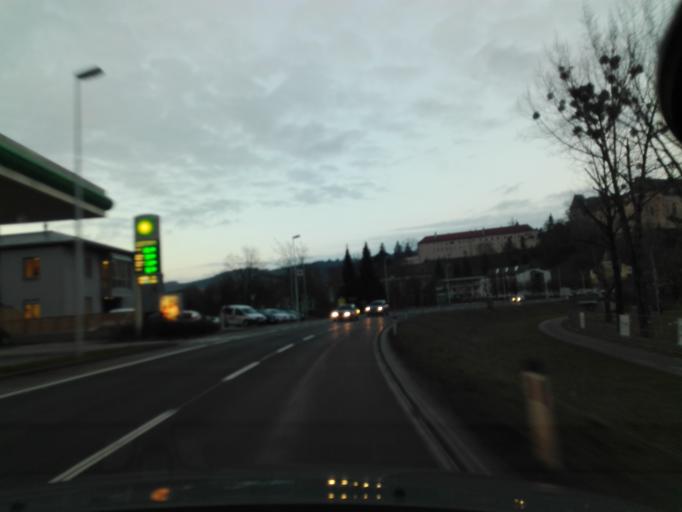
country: AT
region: Upper Austria
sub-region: Politischer Bezirk Perg
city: Bad Kreuzen
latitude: 48.2229
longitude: 14.8506
